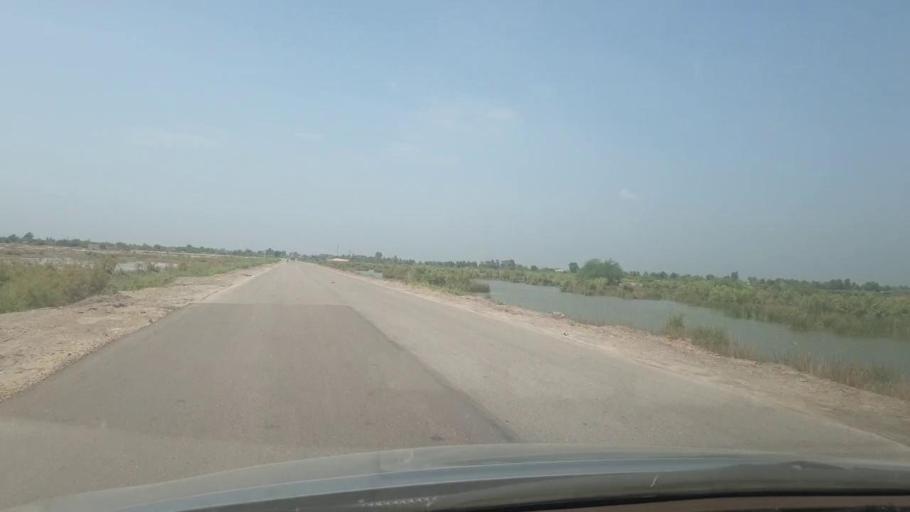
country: PK
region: Sindh
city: Bozdar
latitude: 27.2348
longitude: 68.5705
